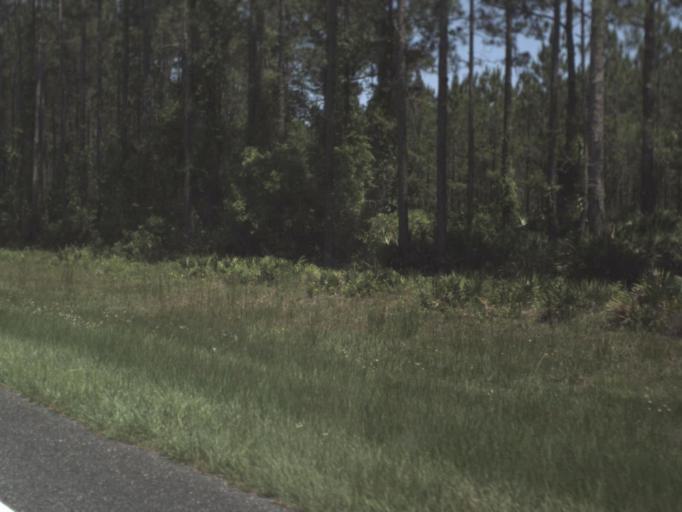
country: US
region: Florida
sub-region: Union County
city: Lake Butler
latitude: 30.2259
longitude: -82.3407
